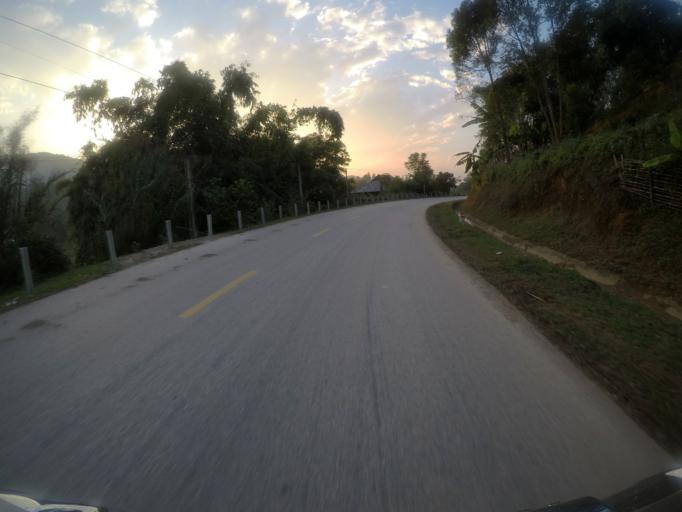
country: VN
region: Lai Chau
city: Than Uyen
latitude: 22.1240
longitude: 103.8002
